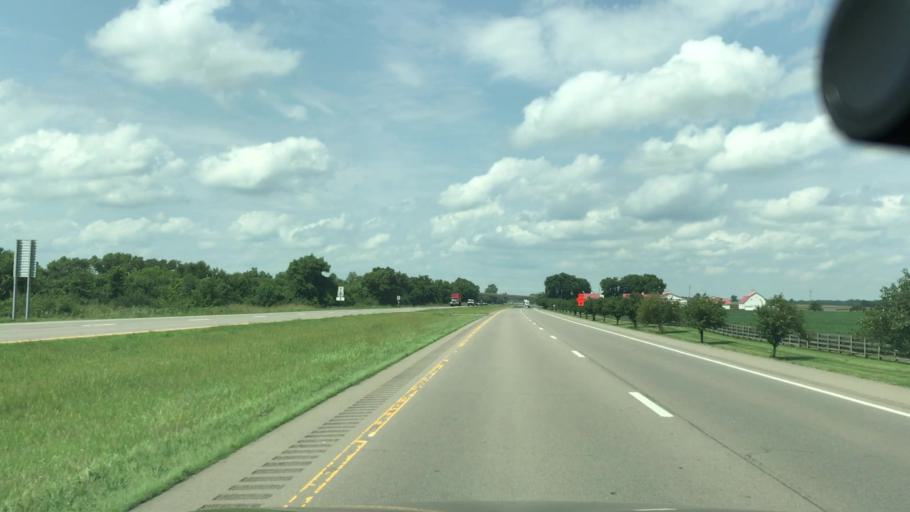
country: US
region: Ohio
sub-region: Ross County
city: Kingston
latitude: 39.4741
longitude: -82.9708
